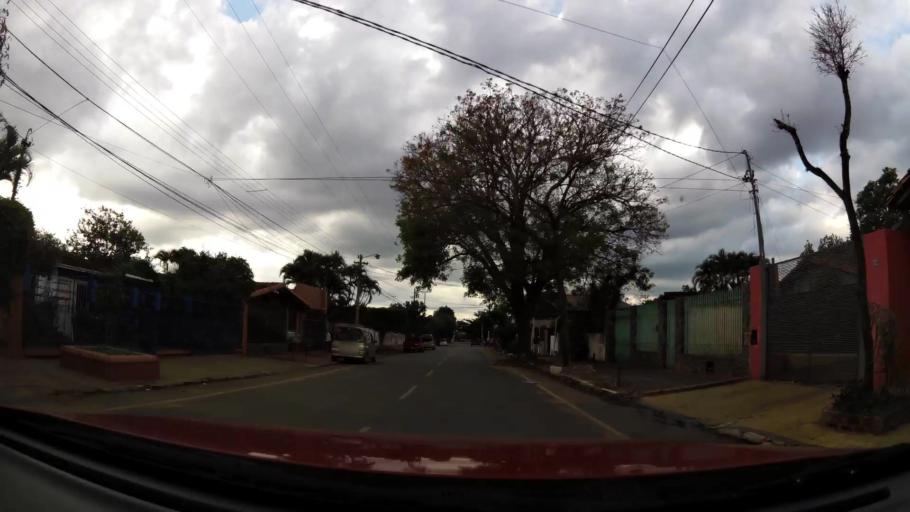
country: PY
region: Central
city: Fernando de la Mora
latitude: -25.3309
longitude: -57.5552
